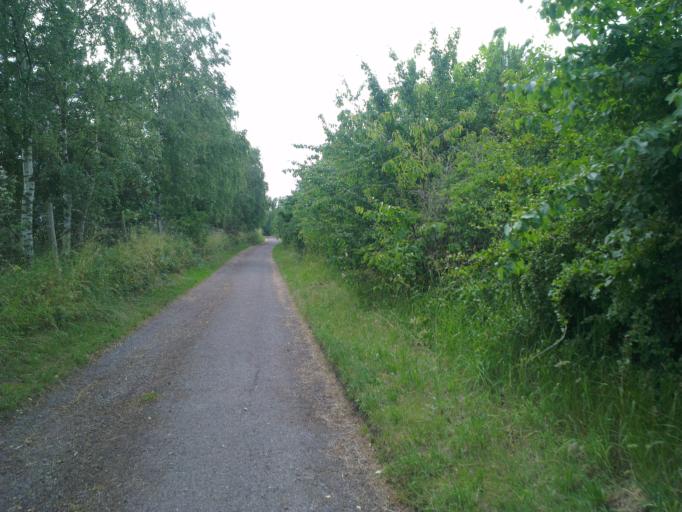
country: DK
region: Capital Region
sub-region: Frederikssund Kommune
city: Skibby
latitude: 55.7418
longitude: 11.9849
